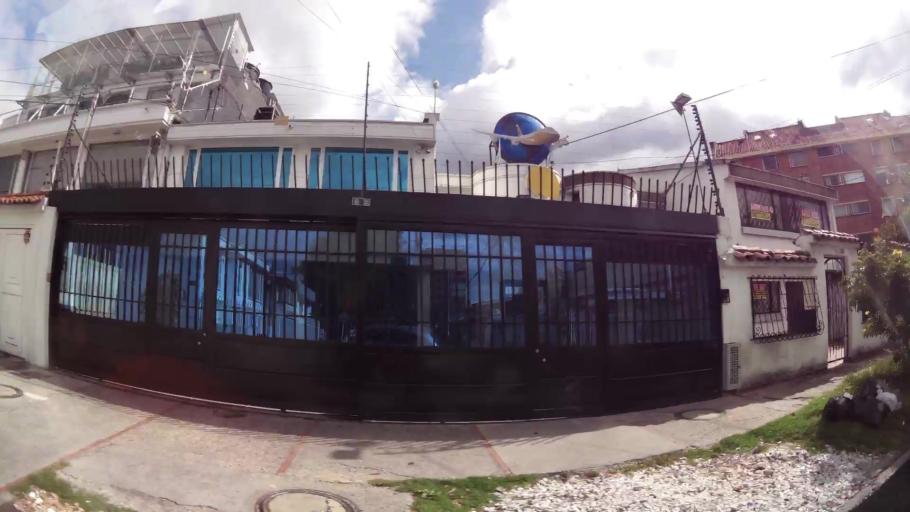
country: CO
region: Bogota D.C.
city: Barrio San Luis
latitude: 4.6897
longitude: -74.0602
